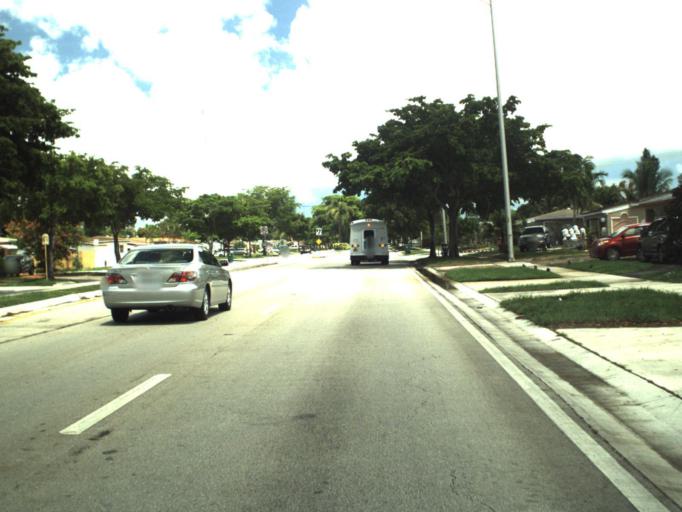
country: US
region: Florida
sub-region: Broward County
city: Miramar
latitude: 25.9815
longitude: -80.2426
